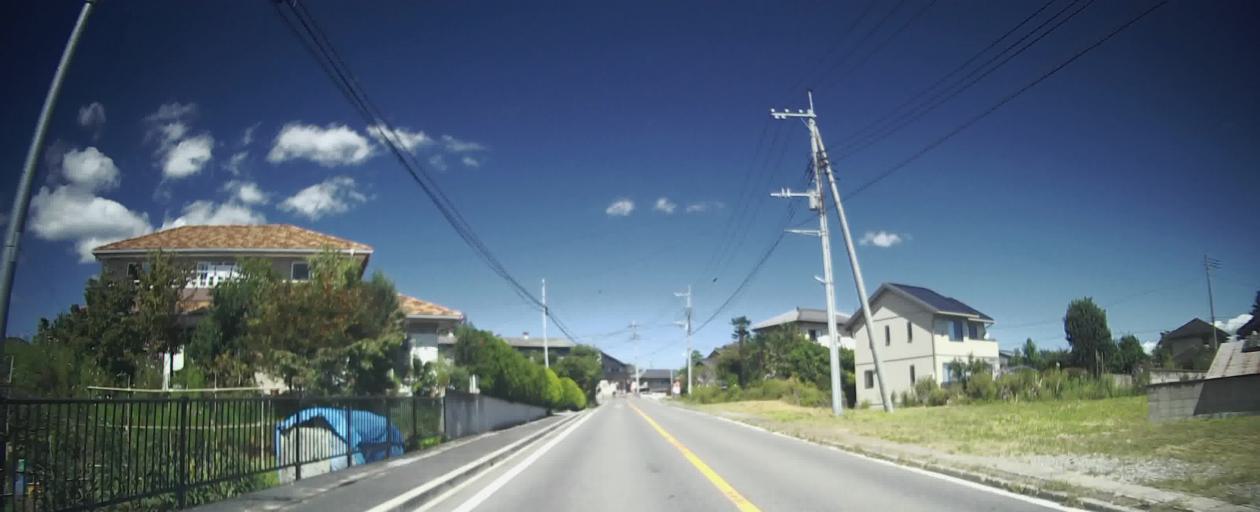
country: JP
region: Gunma
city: Kanekomachi
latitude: 36.4032
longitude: 138.9562
